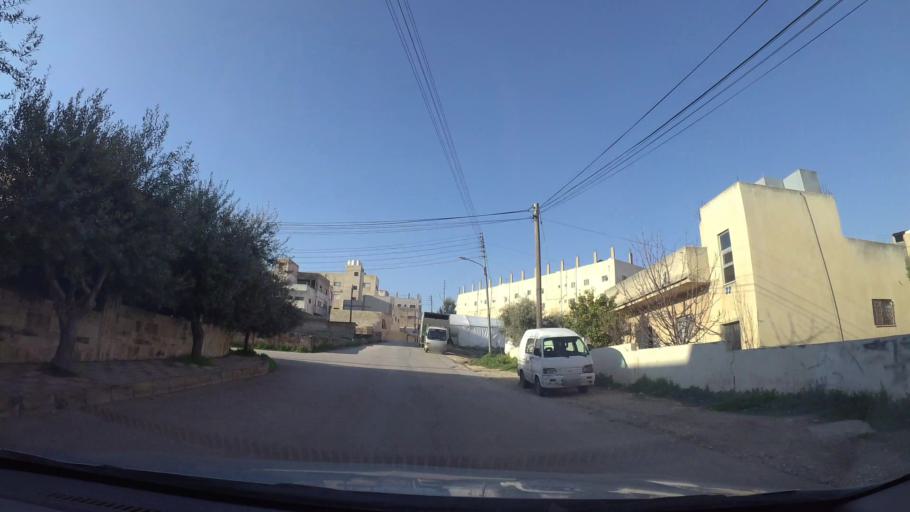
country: JO
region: Amman
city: Al Bunayyat ash Shamaliyah
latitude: 31.8987
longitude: 35.9121
